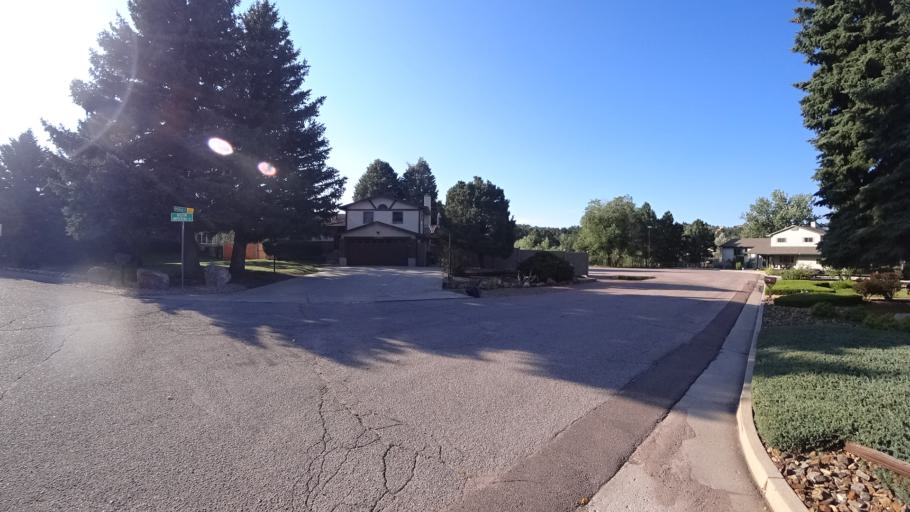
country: US
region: Colorado
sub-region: El Paso County
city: Air Force Academy
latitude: 38.9284
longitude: -104.8024
